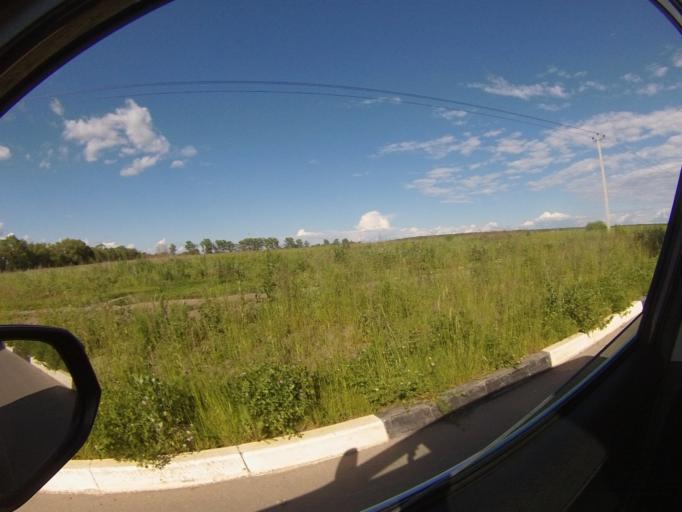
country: RU
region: Orjol
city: Mtsensk
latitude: 53.2944
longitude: 36.6069
